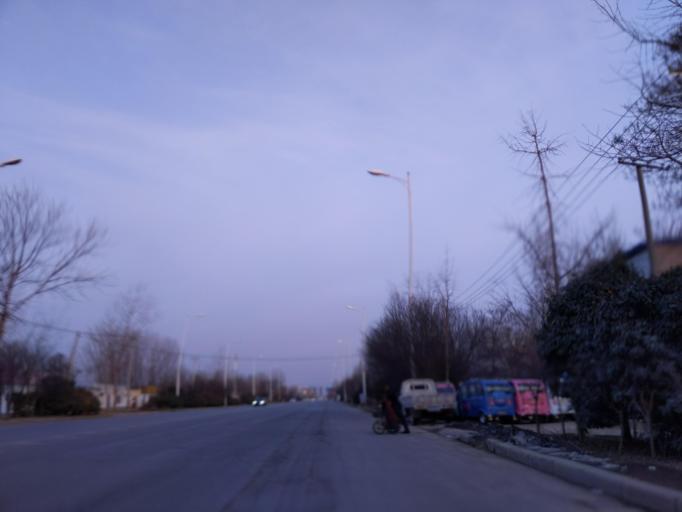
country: CN
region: Henan Sheng
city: Zhongyuanlu
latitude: 35.7872
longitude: 115.1224
